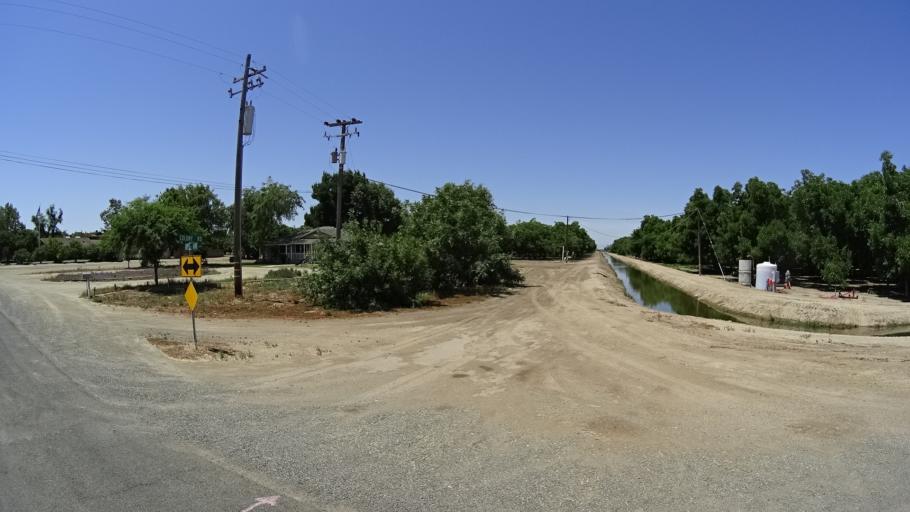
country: US
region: California
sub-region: Kings County
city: Lemoore
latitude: 36.3390
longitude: -119.7627
